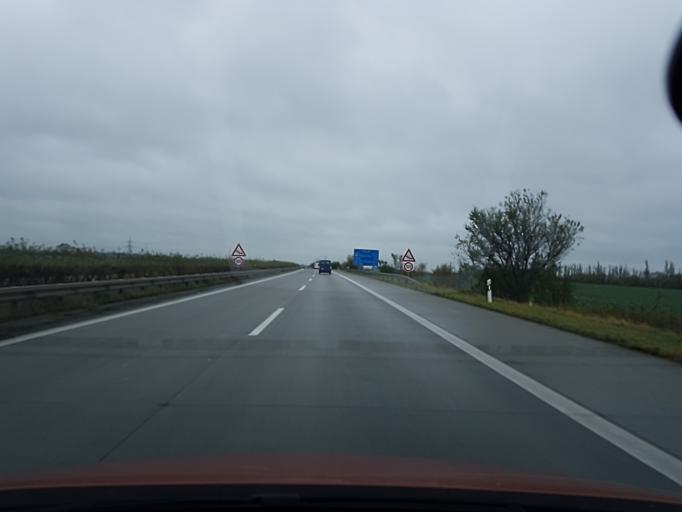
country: DE
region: Mecklenburg-Vorpommern
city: Roggentin
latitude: 54.0711
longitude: 12.1943
